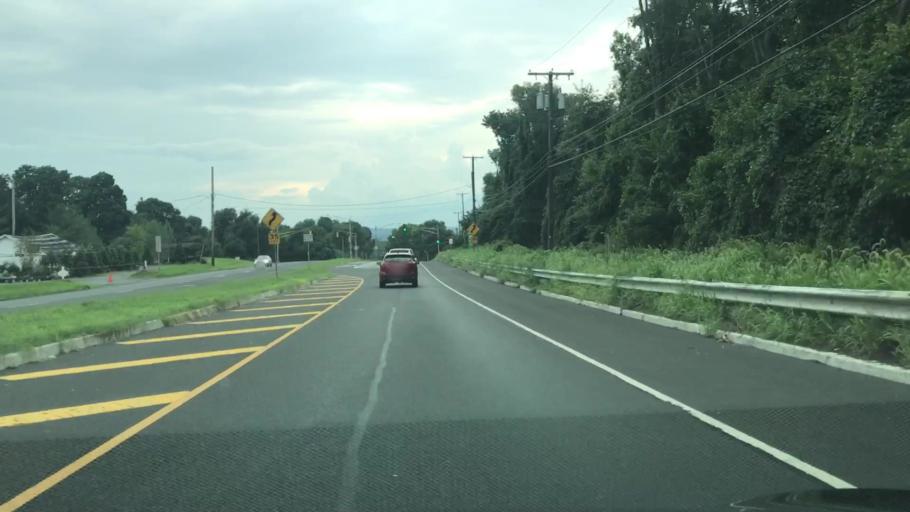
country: US
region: New Jersey
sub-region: Hunterdon County
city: Annandale
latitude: 40.6422
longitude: -74.8659
